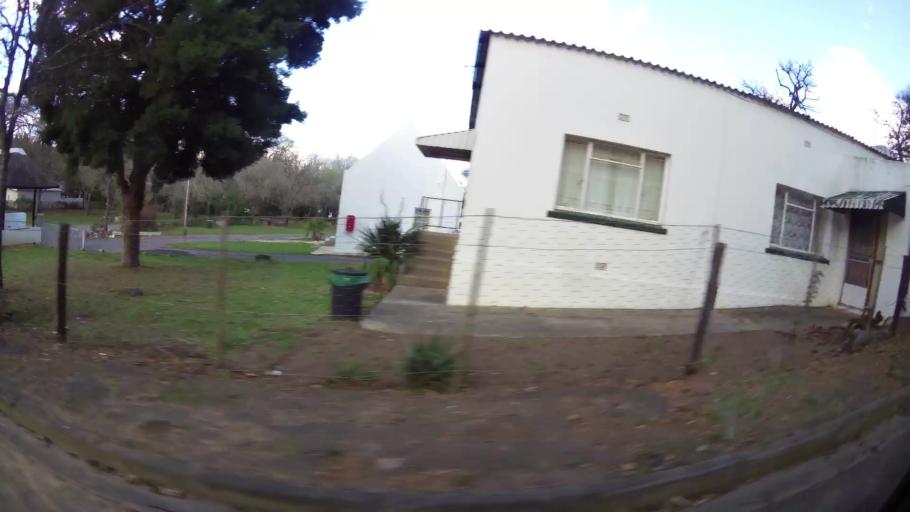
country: ZA
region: Western Cape
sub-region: Overberg District Municipality
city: Swellendam
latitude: -34.0130
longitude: 20.4494
